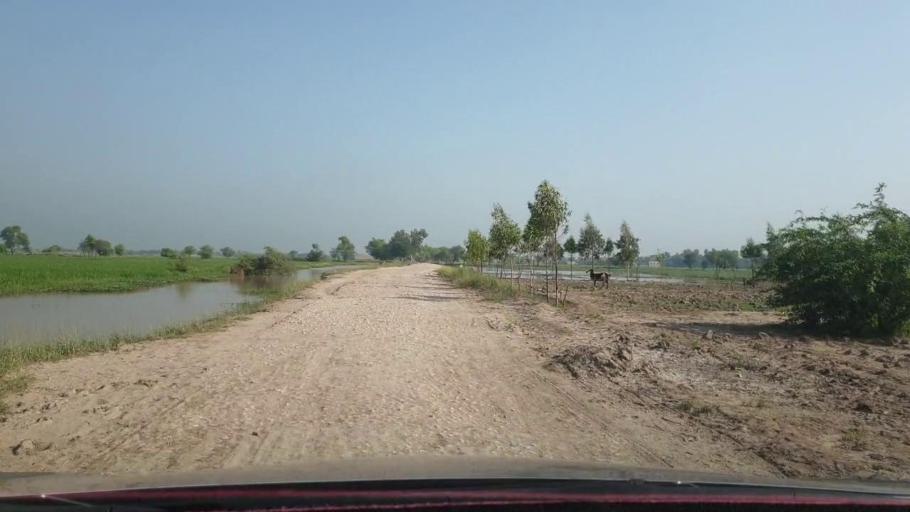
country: PK
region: Sindh
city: Nasirabad
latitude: 27.4556
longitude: 67.9176
